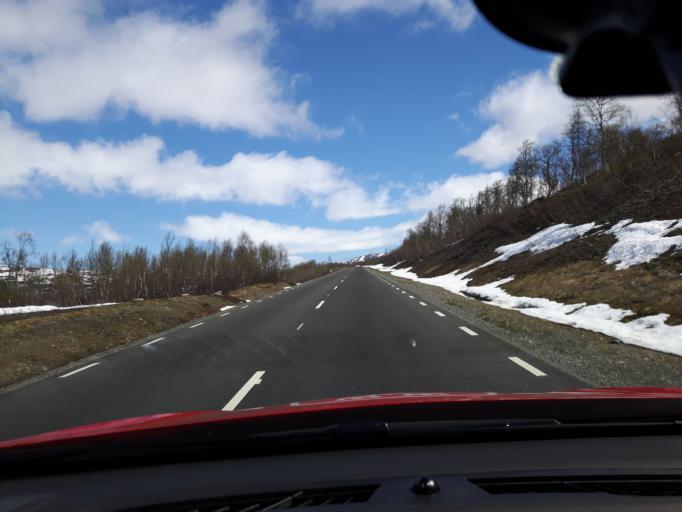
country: NO
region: Nordland
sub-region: Hattfjelldal
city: Hattfjelldal
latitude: 64.9915
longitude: 14.2246
